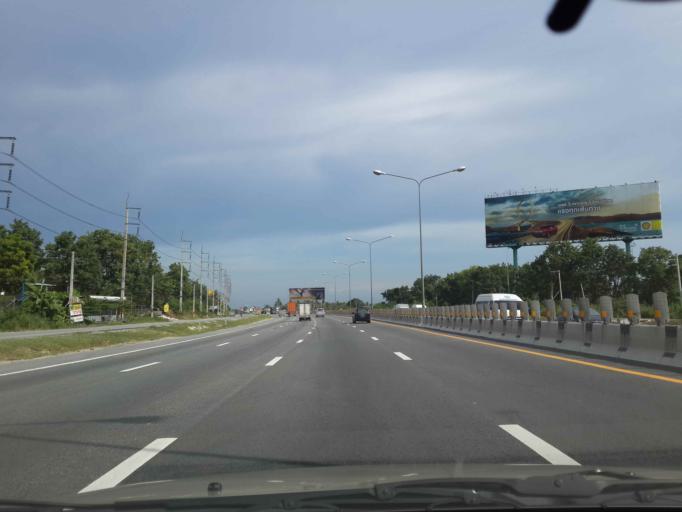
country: TH
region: Chon Buri
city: Chon Buri
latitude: 13.2600
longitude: 100.9900
